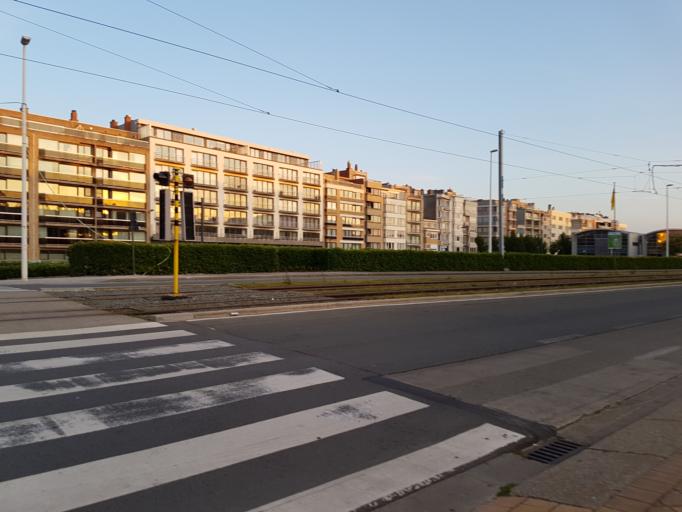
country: BE
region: Flanders
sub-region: Provincie West-Vlaanderen
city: Ostend
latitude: 51.2262
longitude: 2.9057
